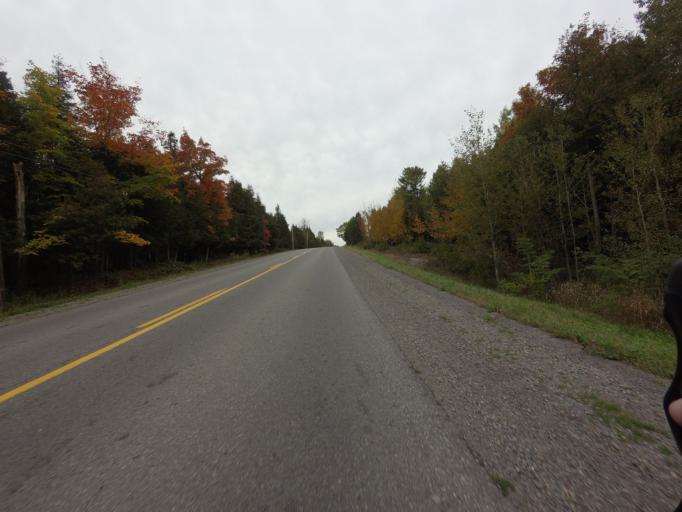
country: CA
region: Ontario
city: Brockville
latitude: 44.7882
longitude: -75.7731
